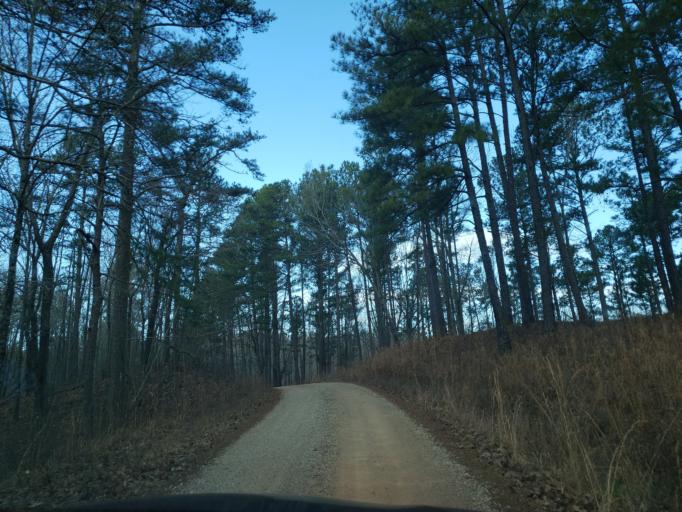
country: US
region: Alabama
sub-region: Cleburne County
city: Heflin
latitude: 33.6804
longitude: -85.6310
